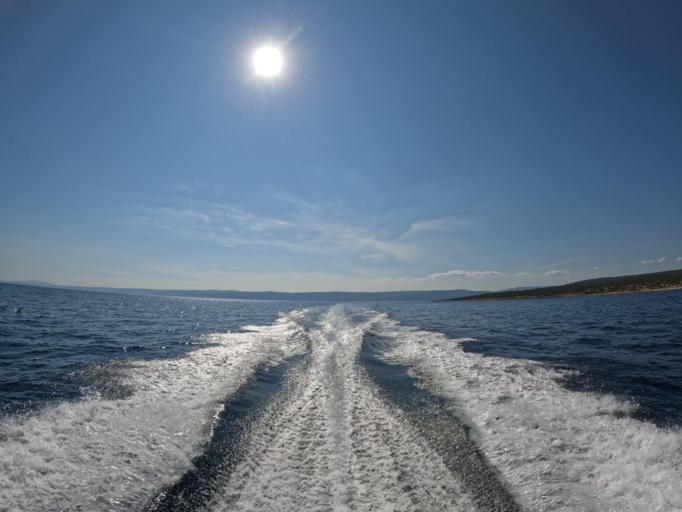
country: HR
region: Primorsko-Goranska
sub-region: Grad Krk
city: Krk
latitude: 44.9519
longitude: 14.5538
